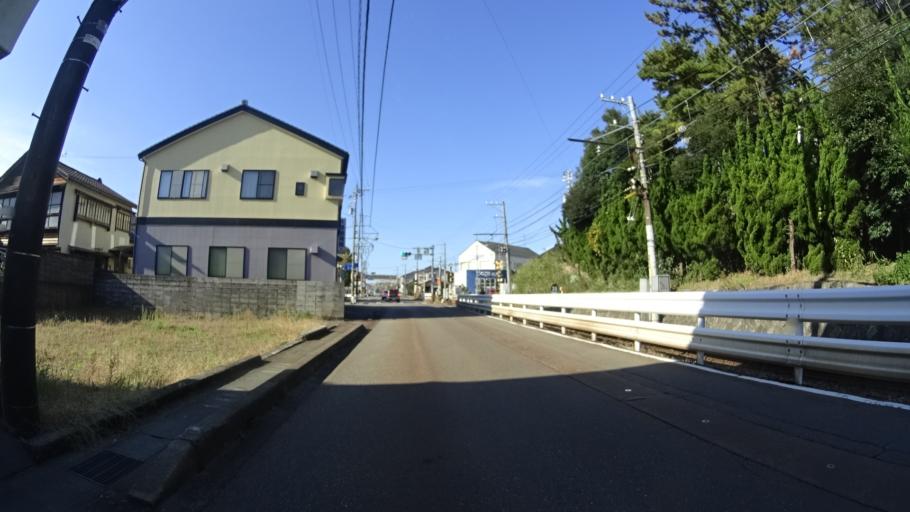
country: JP
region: Ishikawa
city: Kanazawa-shi
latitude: 36.6309
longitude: 136.6374
